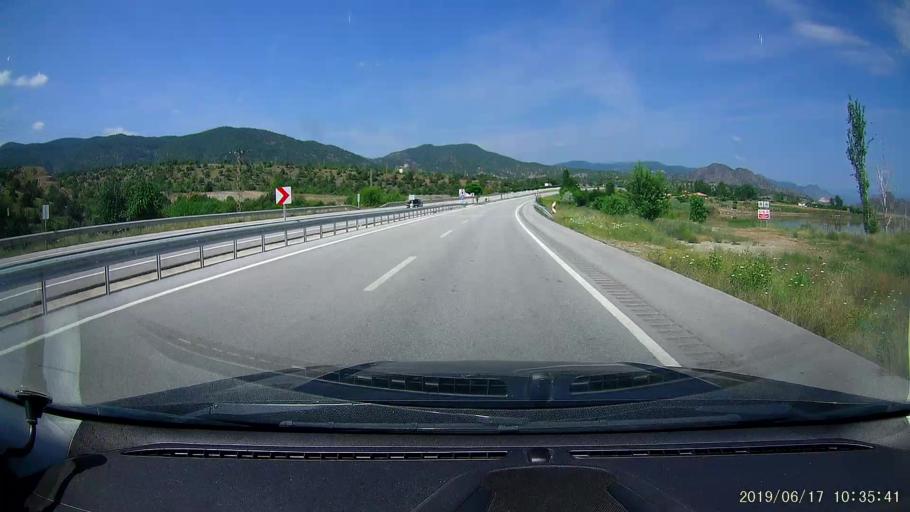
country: TR
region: Corum
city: Osmancik
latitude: 40.9716
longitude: 34.6978
